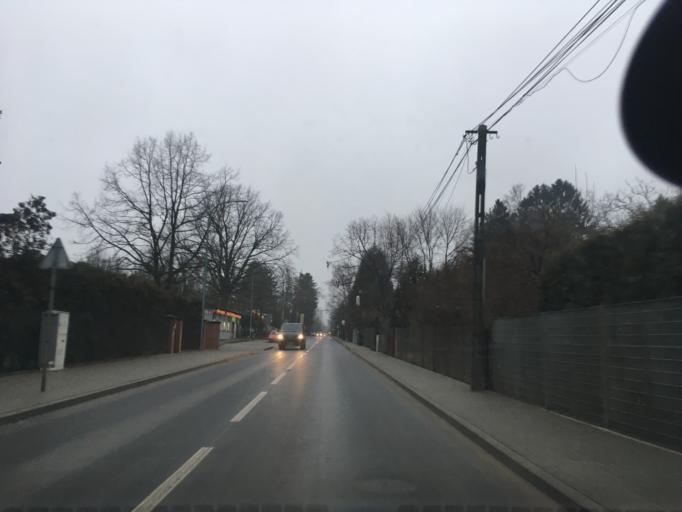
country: PL
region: Masovian Voivodeship
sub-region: Powiat piaseczynski
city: Piaseczno
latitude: 52.0516
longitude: 20.9873
